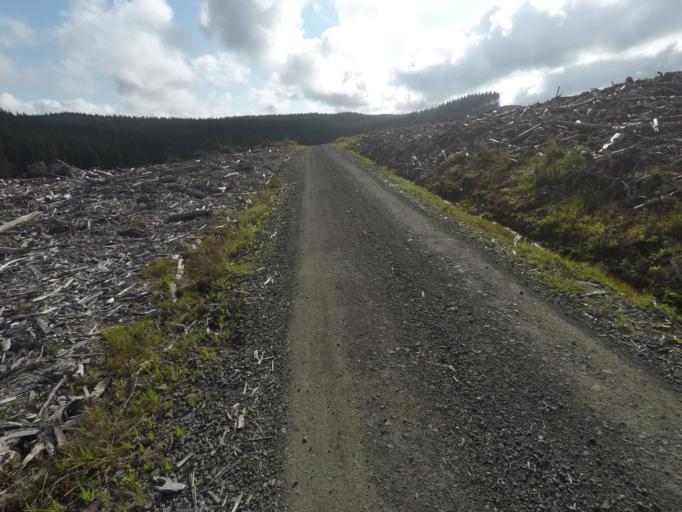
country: NZ
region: Auckland
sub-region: Auckland
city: Parakai
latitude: -36.7133
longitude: 174.5686
